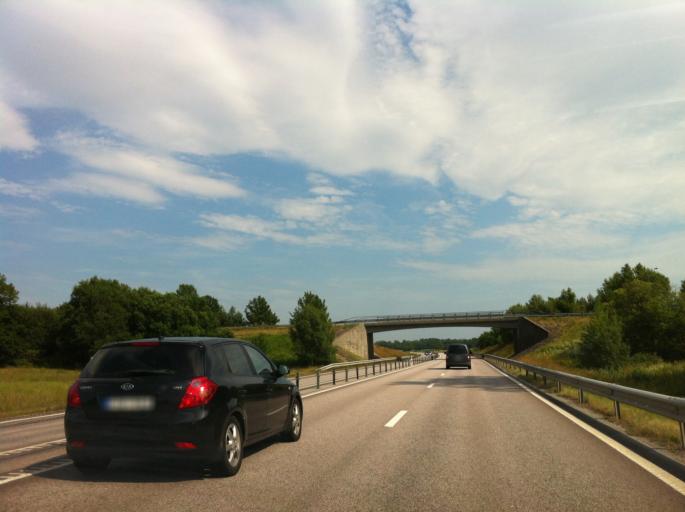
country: SE
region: Kalmar
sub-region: Kalmar Kommun
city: Ljungbyholm
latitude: 56.6779
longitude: 16.2049
